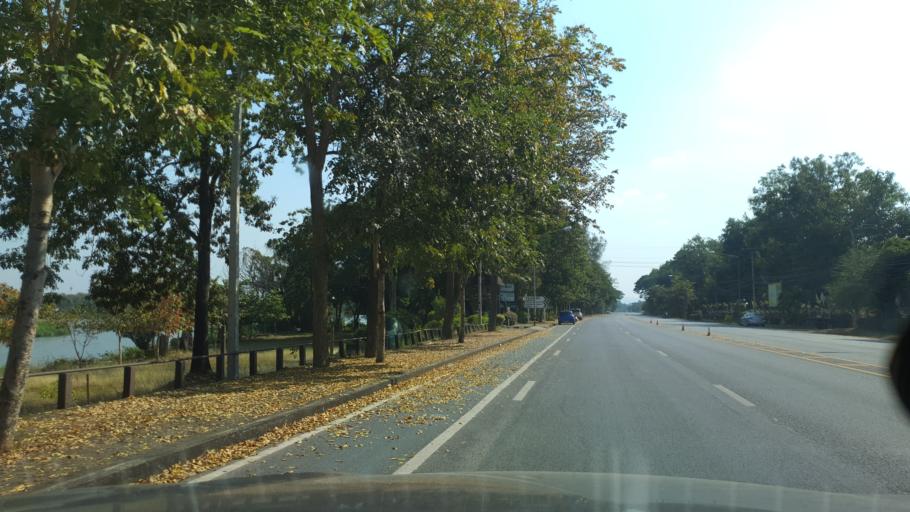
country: TH
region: Tak
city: Tak
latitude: 16.8706
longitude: 99.1187
